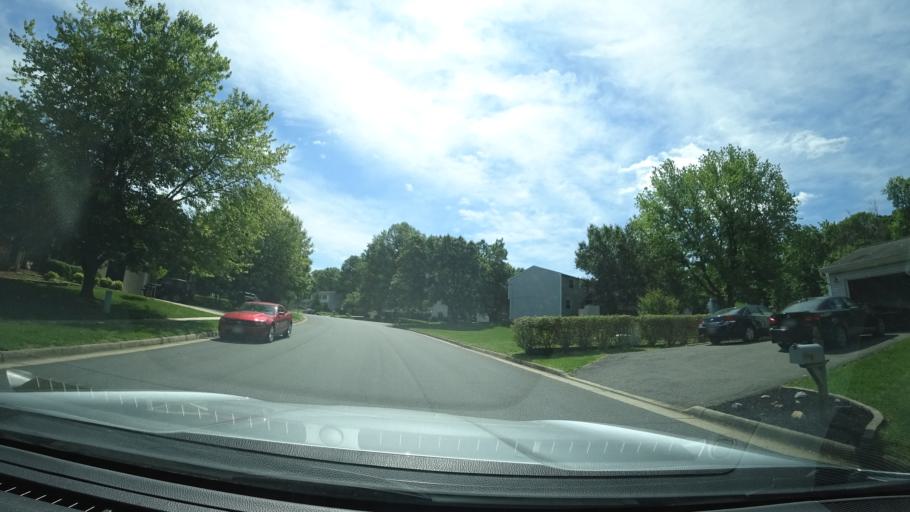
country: US
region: Virginia
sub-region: Loudoun County
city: Oak Grove
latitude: 38.9873
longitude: -77.4060
